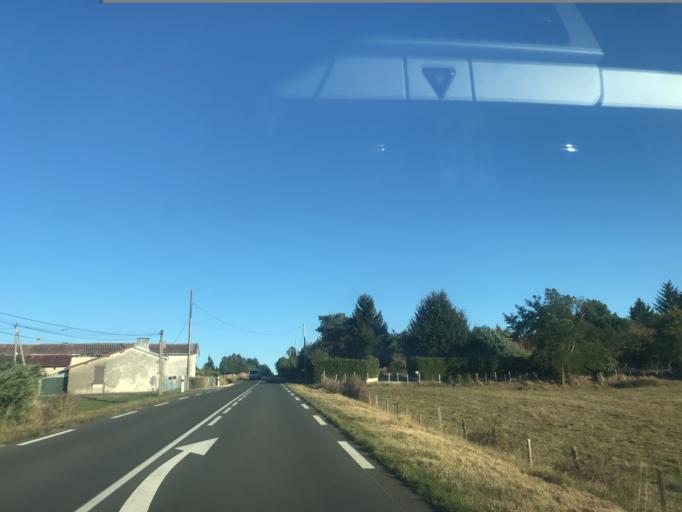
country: FR
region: Poitou-Charentes
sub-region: Departement de la Charente-Maritime
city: Saint-Aigulin
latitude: 45.1692
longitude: -0.0513
